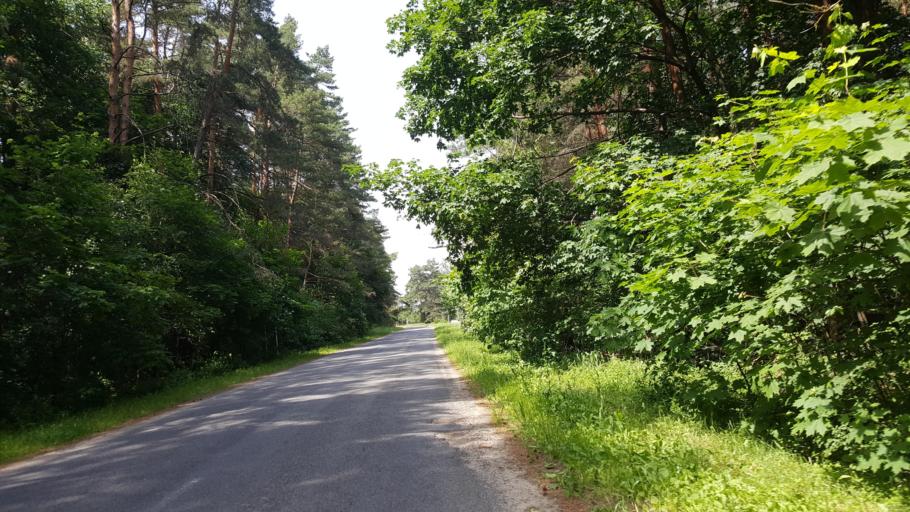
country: BY
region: Brest
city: Kamyanyuki
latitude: 52.5028
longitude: 23.8628
